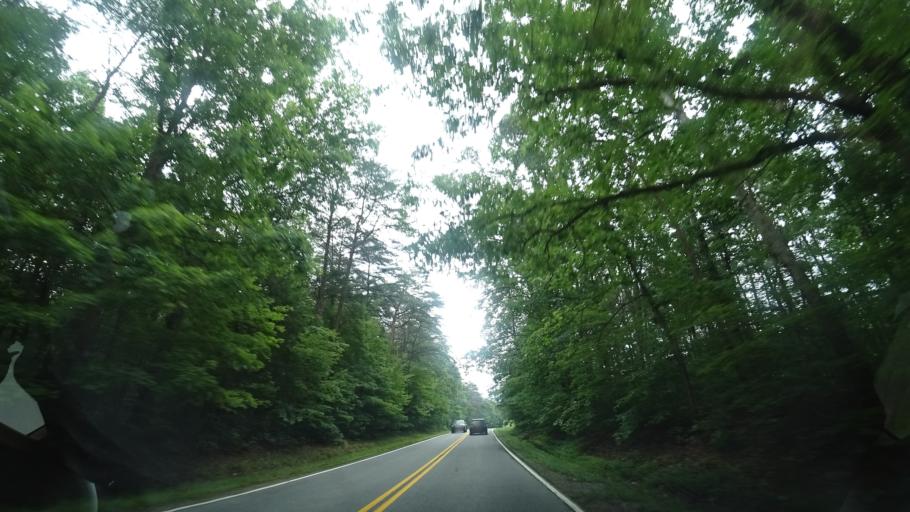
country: US
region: Virginia
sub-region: Spotsylvania County
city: Spotsylvania
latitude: 38.1319
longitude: -77.7871
